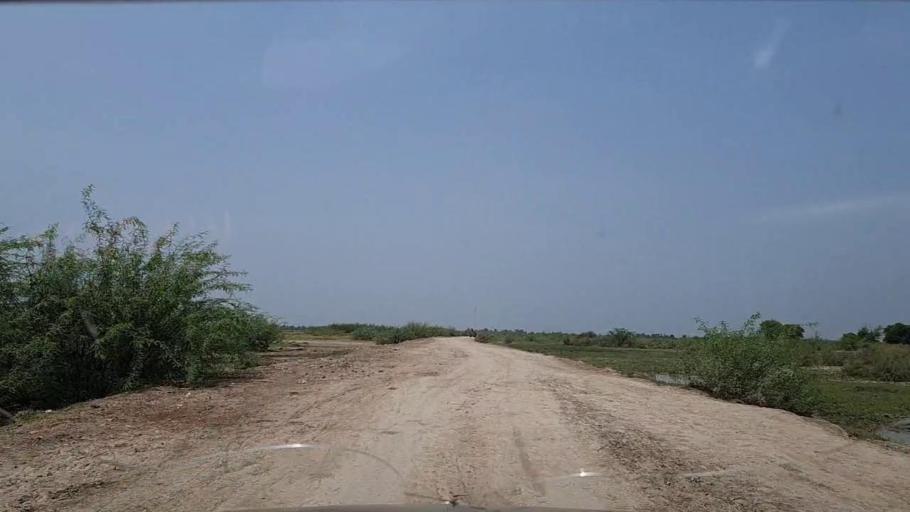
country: PK
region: Sindh
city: Adilpur
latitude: 27.9074
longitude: 69.2209
